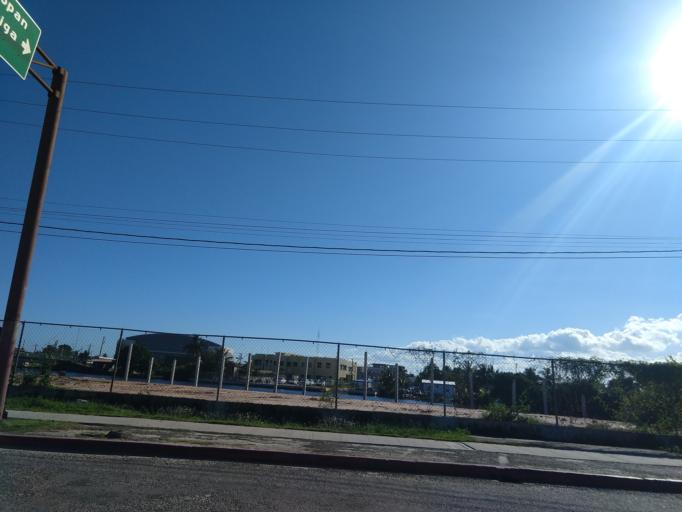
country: BZ
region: Belize
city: Belize City
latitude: 17.5042
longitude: -88.1981
